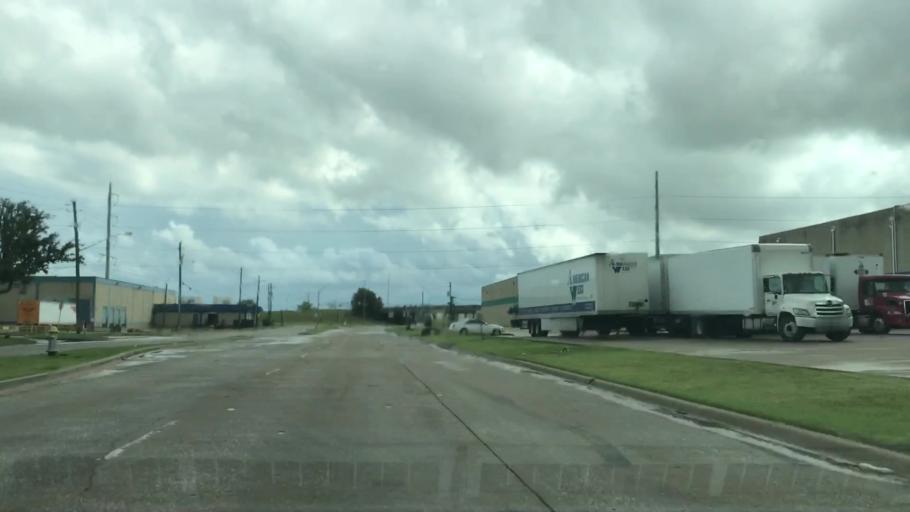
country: US
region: Texas
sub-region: Dallas County
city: Irving
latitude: 32.8111
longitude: -96.9003
